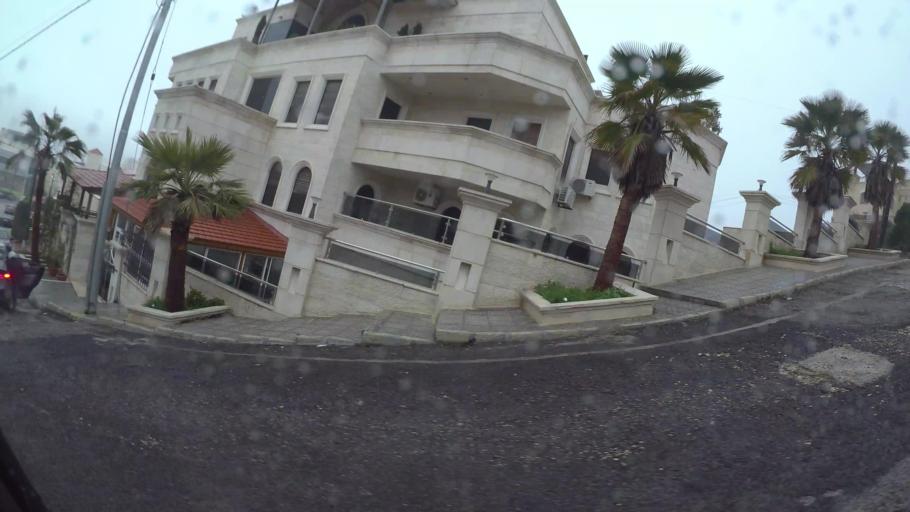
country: JO
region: Amman
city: Wadi as Sir
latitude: 31.9992
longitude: 35.8207
